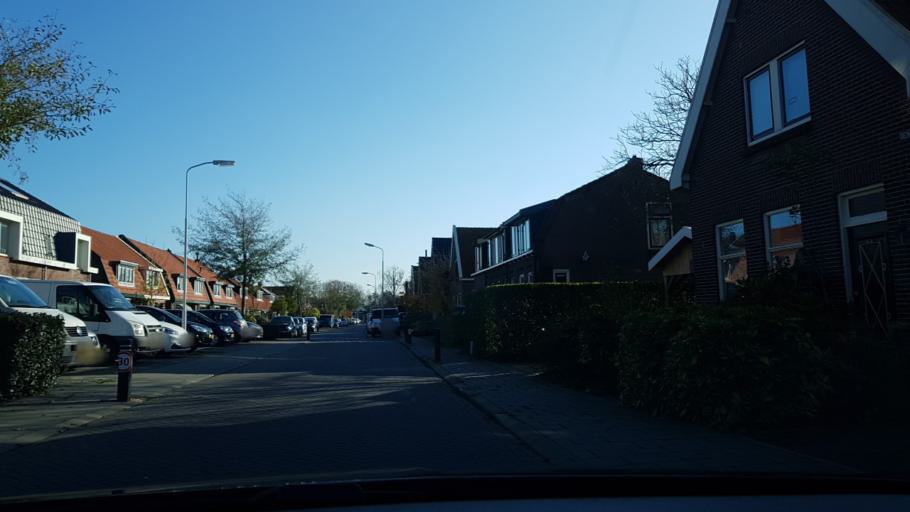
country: NL
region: North Holland
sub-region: Gemeente Uitgeest
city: Uitgeest
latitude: 52.4648
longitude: 4.7354
